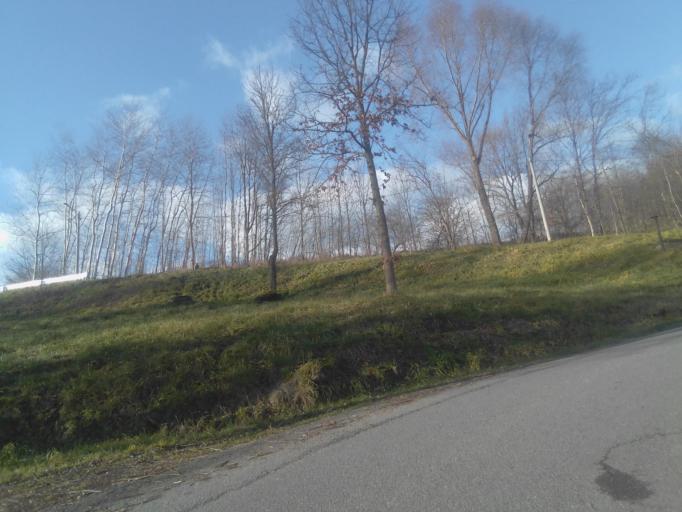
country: PL
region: Subcarpathian Voivodeship
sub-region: Powiat rzeszowski
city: Lubenia
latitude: 49.9369
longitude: 21.9016
